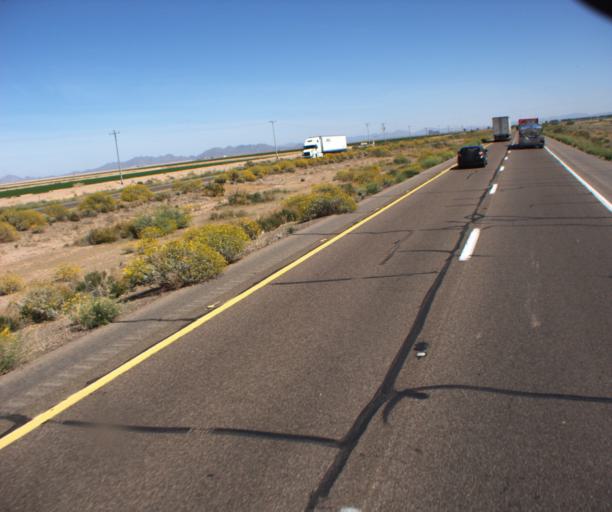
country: US
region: Arizona
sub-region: Maricopa County
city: Gila Bend
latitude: 32.9135
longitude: -112.9424
